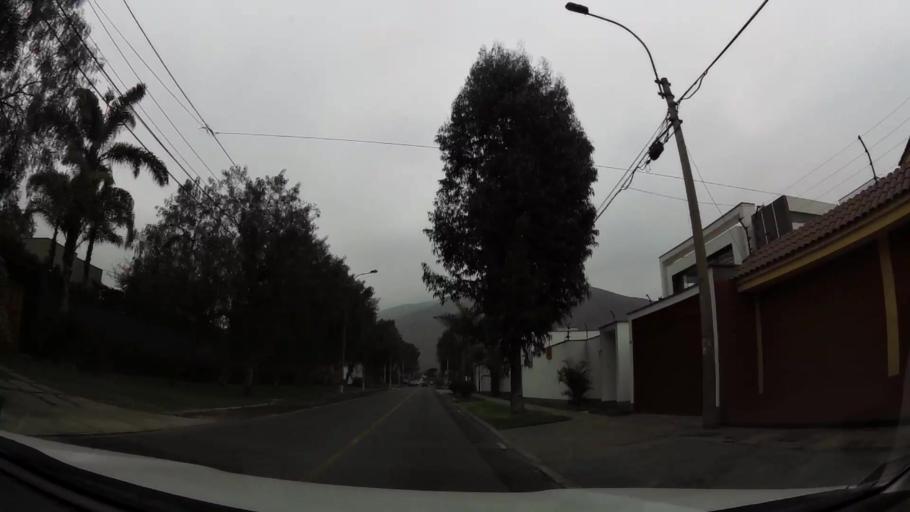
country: PE
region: Lima
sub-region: Lima
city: La Molina
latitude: -12.0793
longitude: -76.9156
